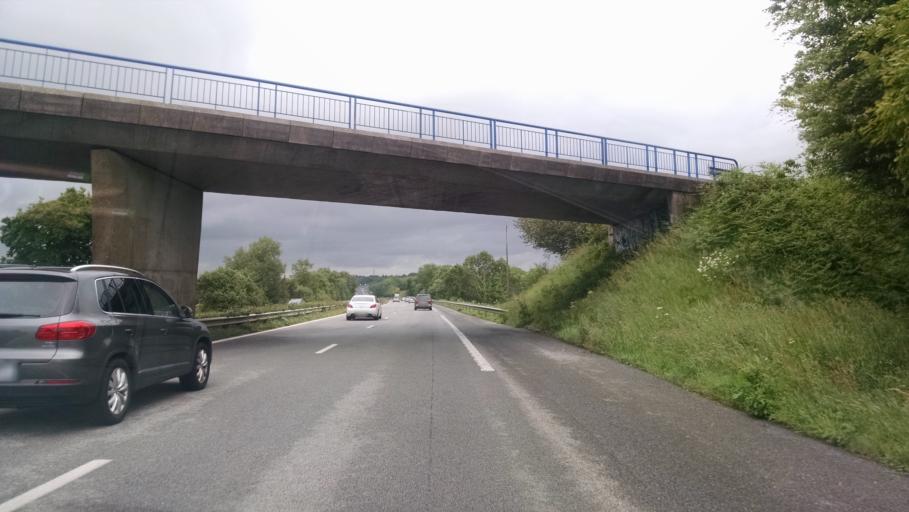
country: FR
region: Brittany
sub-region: Departement du Finistere
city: Melgven
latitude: 47.8982
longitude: -3.8308
